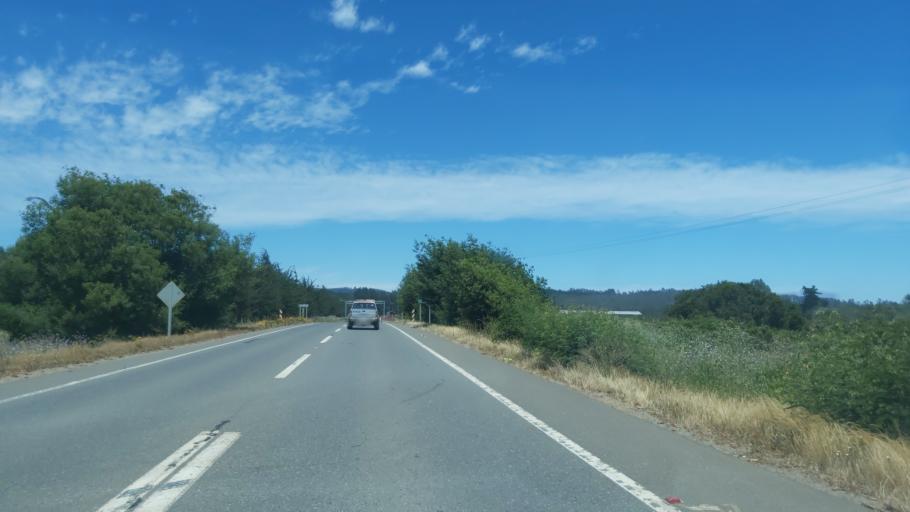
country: CL
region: Maule
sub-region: Provincia de Talca
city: Constitucion
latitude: -35.3066
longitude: -72.3789
